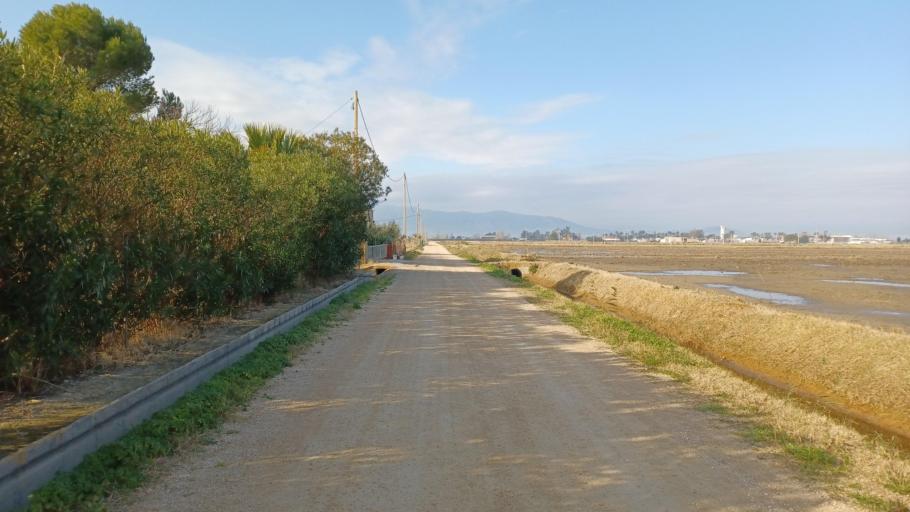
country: ES
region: Catalonia
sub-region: Provincia de Tarragona
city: Deltebre
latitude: 40.6422
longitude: 0.6985
